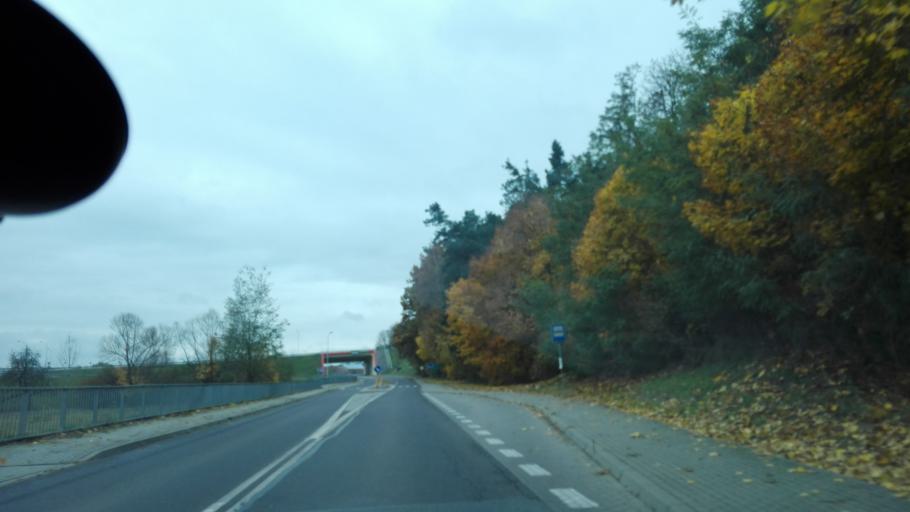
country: PL
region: Lublin Voivodeship
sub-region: Powiat pulawski
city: Pulawy
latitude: 51.4395
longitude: 21.9106
